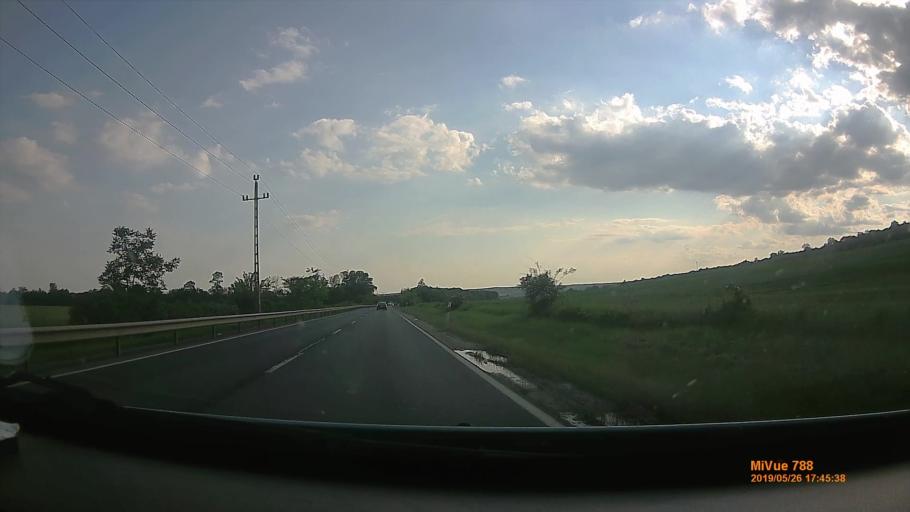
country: HU
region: Borsod-Abauj-Zemplen
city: Aszalo
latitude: 48.2155
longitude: 20.9473
